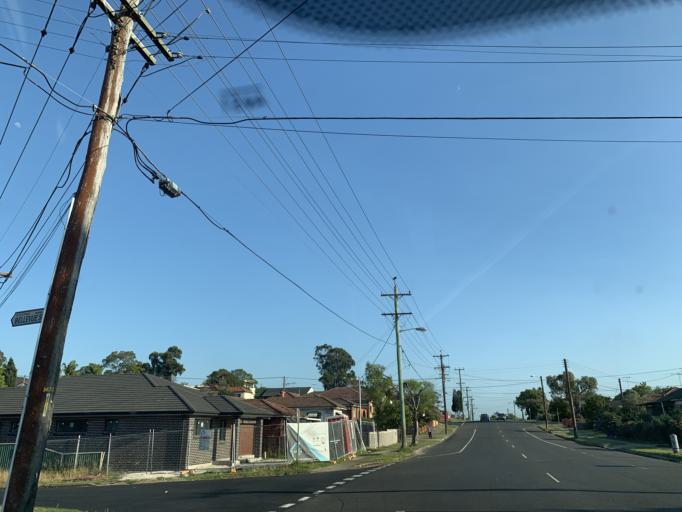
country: AU
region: New South Wales
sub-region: Blacktown
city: Blacktown
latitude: -33.7806
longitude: 150.8943
